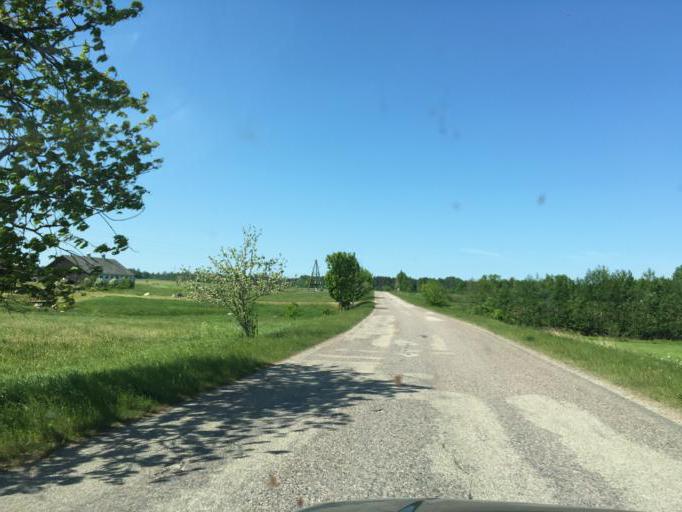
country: LV
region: Dundaga
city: Dundaga
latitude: 57.4665
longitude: 22.3227
